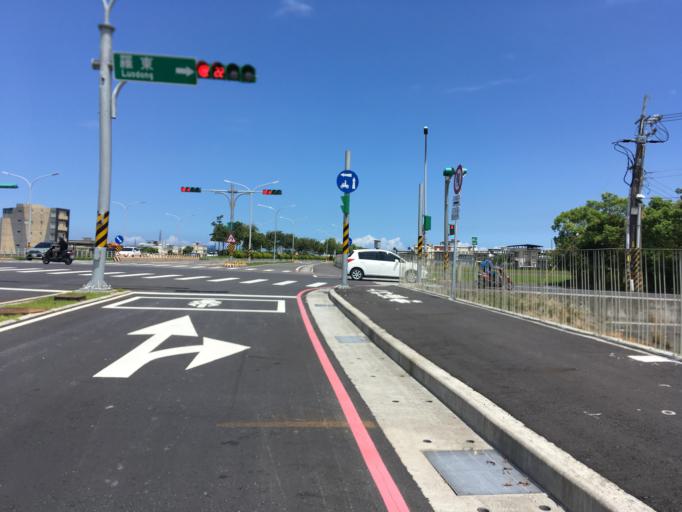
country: TW
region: Taiwan
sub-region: Yilan
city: Yilan
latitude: 24.6934
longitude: 121.7803
